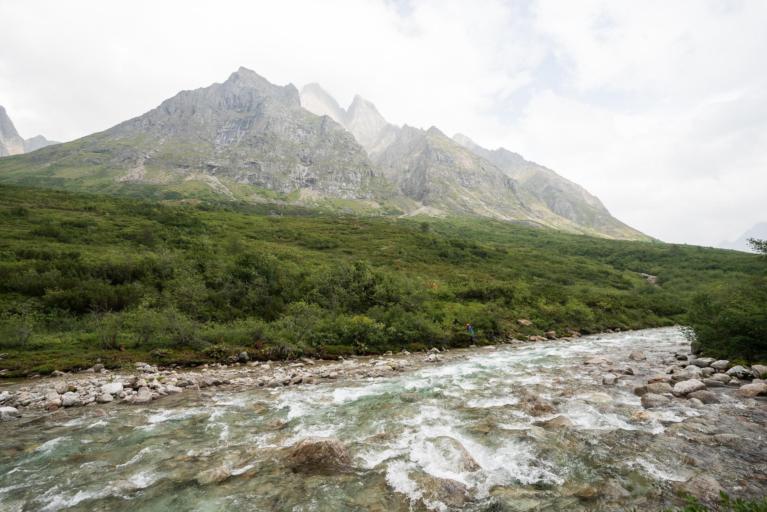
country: RU
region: Transbaikal Territory
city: Chara
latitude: 56.9353
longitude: 117.6253
